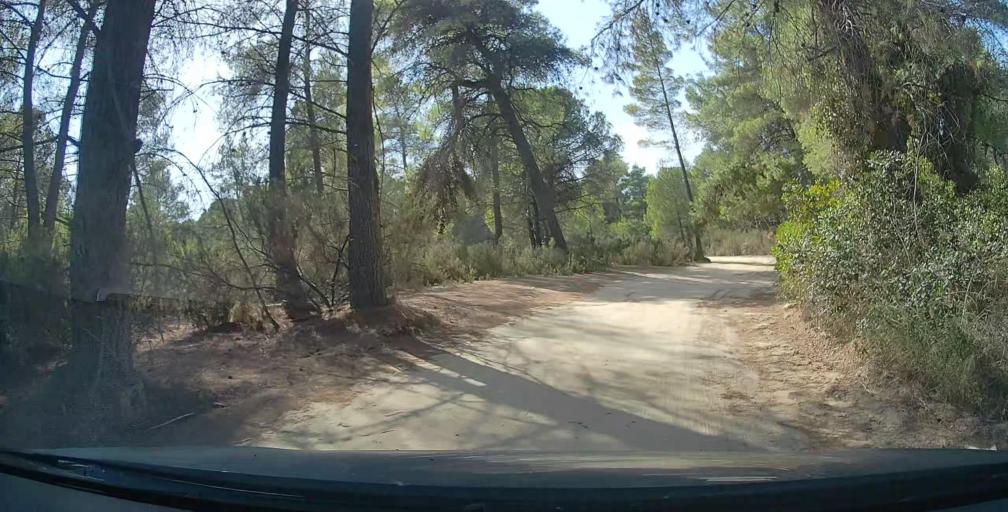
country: GR
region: Central Macedonia
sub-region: Nomos Chalkidikis
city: Sarti
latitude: 40.1291
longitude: 23.9527
